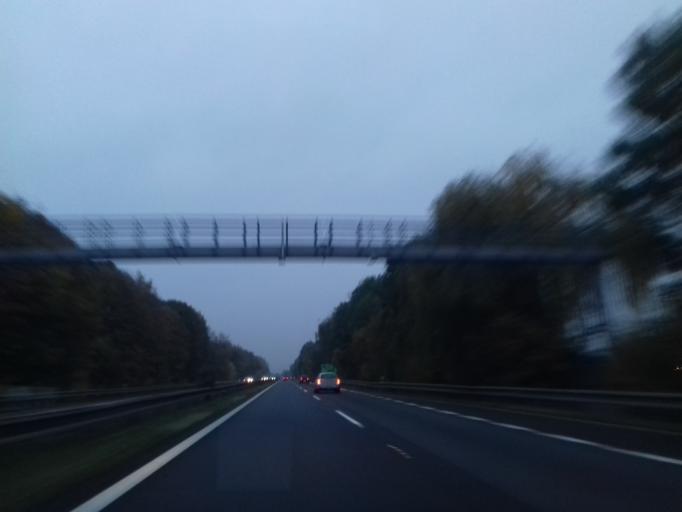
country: CZ
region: Olomoucky
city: Naklo
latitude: 49.6648
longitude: 17.0995
